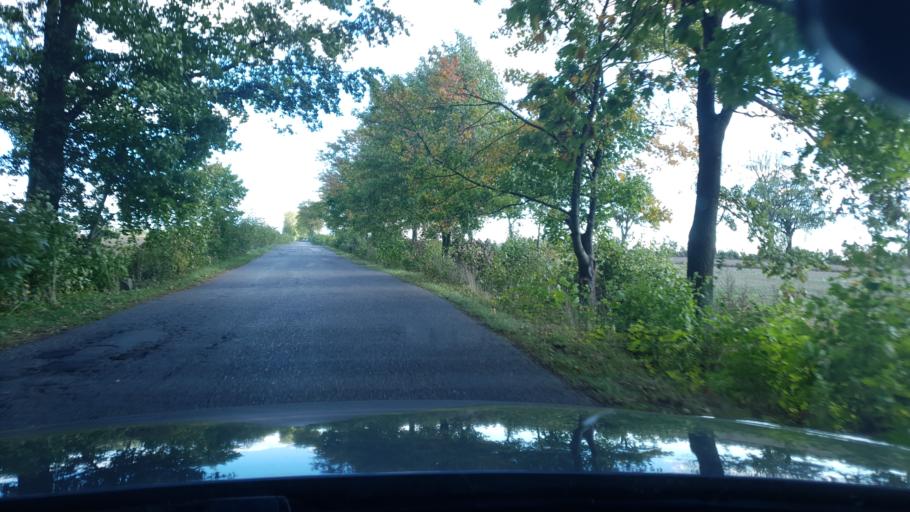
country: PL
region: Pomeranian Voivodeship
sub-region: Powiat pucki
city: Zelistrzewo
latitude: 54.6883
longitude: 18.4296
